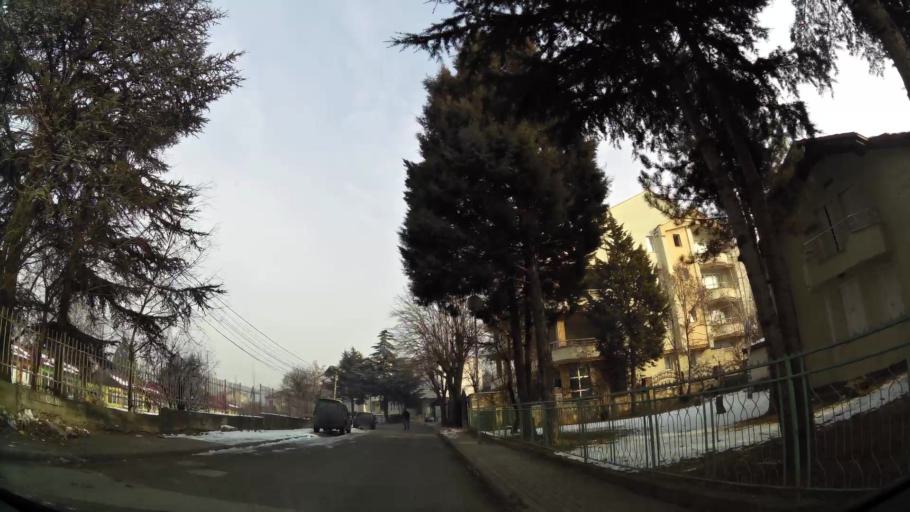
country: MK
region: Butel
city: Butel
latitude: 42.0209
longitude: 21.4532
